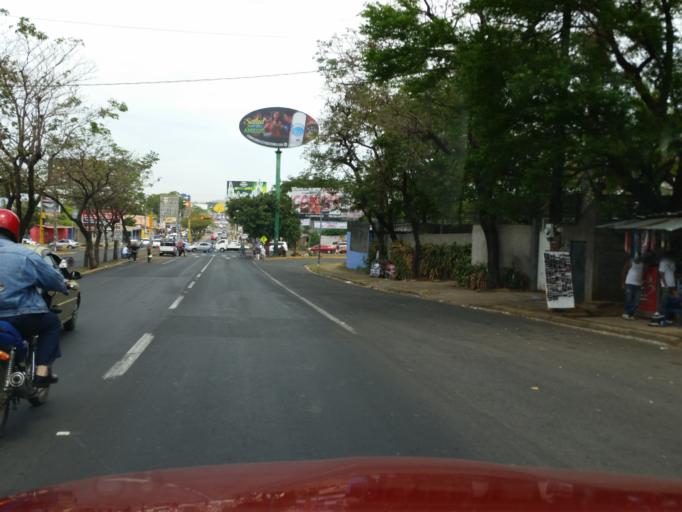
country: NI
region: Managua
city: Managua
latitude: 12.1366
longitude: -86.2744
